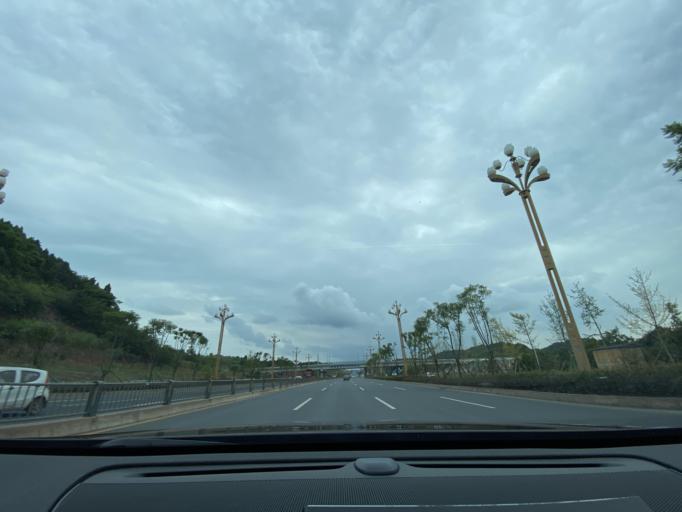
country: CN
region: Sichuan
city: Jiancheng
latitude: 30.4633
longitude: 104.4956
